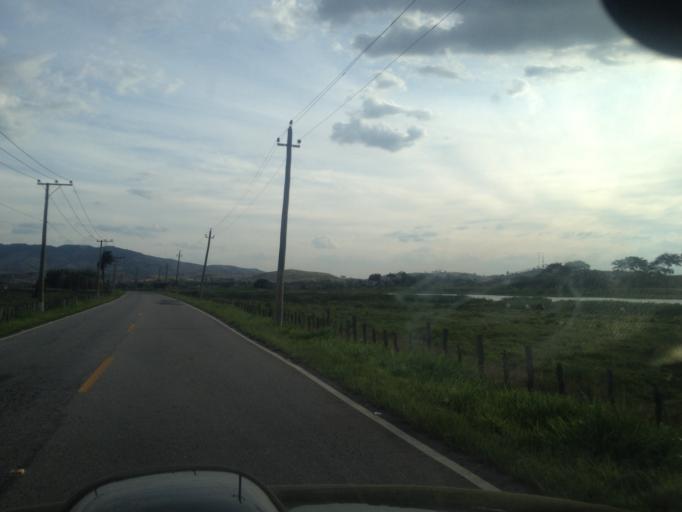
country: BR
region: Rio de Janeiro
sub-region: Porto Real
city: Porto Real
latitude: -22.4319
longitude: -44.2899
